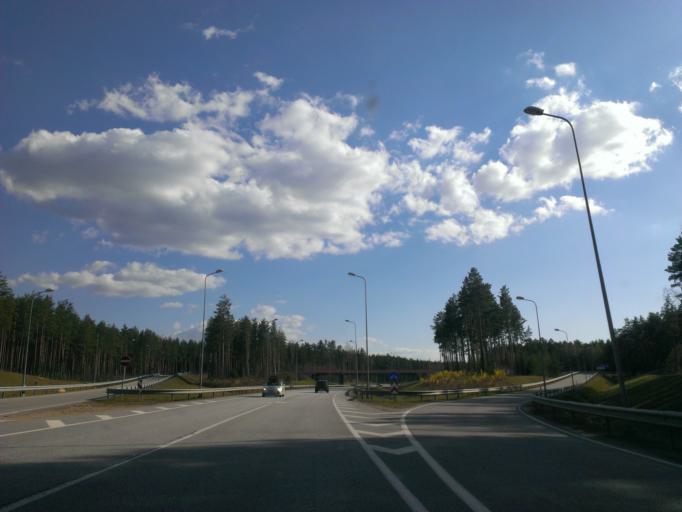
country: LV
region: Saulkrastu
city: Saulkrasti
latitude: 57.2707
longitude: 24.4379
